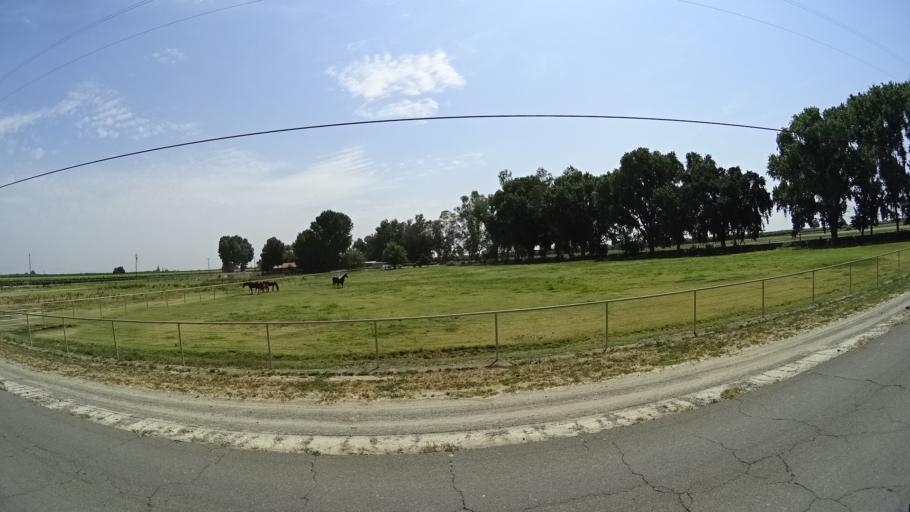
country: US
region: California
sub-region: Kings County
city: Armona
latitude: 36.3634
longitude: -119.7451
